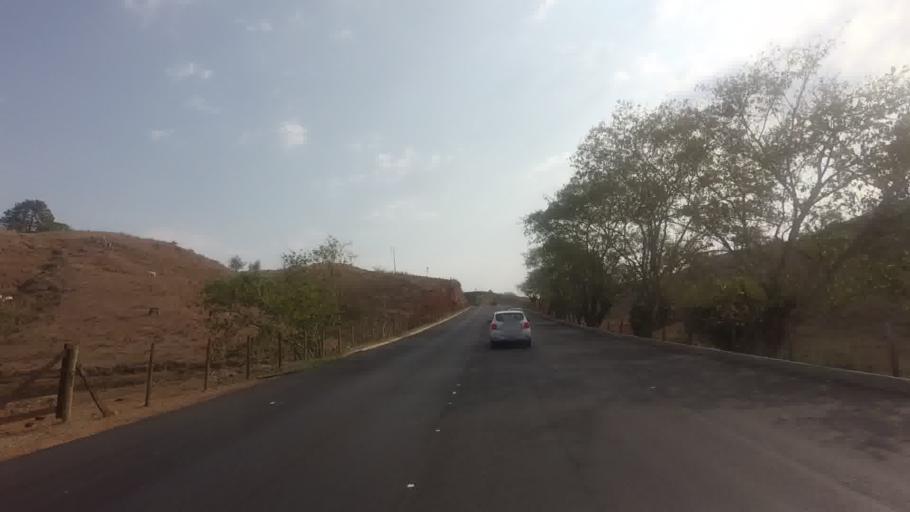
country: BR
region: Rio de Janeiro
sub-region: Bom Jesus Do Itabapoana
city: Bom Jesus do Itabapoana
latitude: -21.1956
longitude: -41.7083
